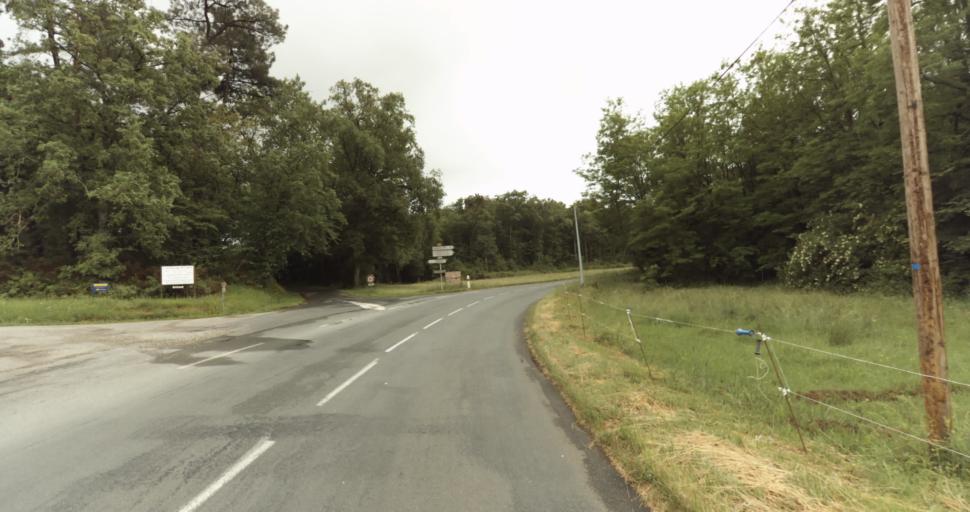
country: FR
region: Aquitaine
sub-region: Departement de la Dordogne
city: Belves
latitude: 44.7093
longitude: 0.9344
